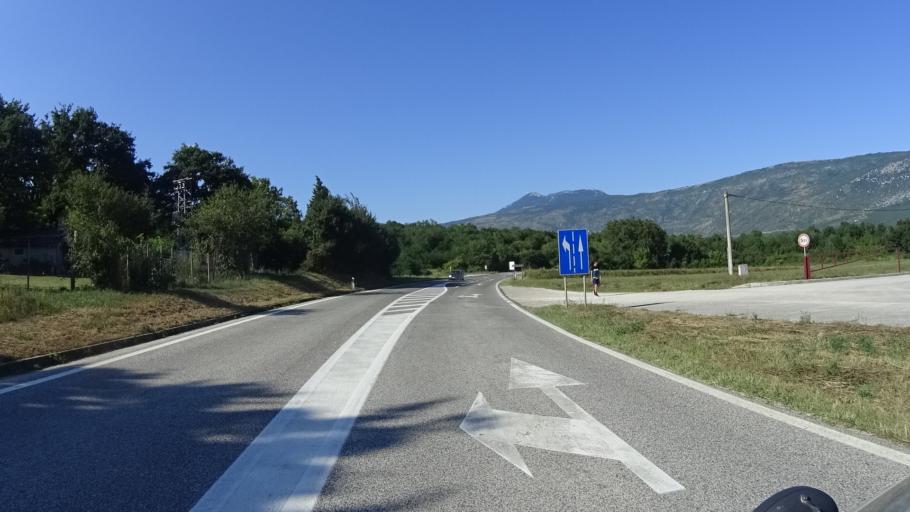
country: HR
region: Istarska
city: Vinez
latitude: 45.2031
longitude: 14.1349
